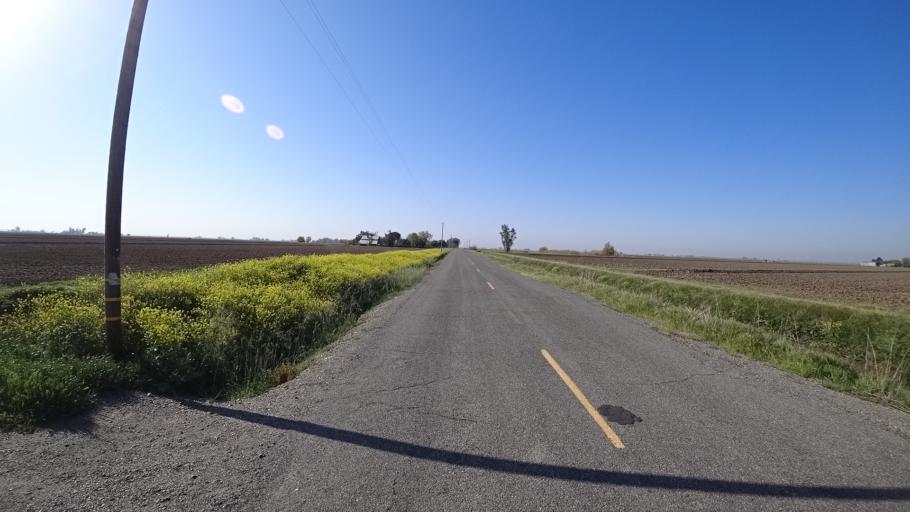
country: US
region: California
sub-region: Glenn County
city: Willows
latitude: 39.5675
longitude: -122.1077
